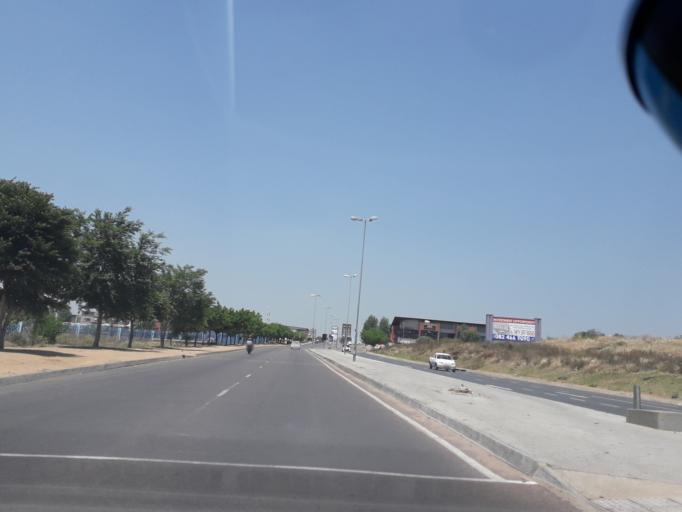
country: ZA
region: Gauteng
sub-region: City of Johannesburg Metropolitan Municipality
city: Midrand
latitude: -25.9736
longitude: 28.1197
